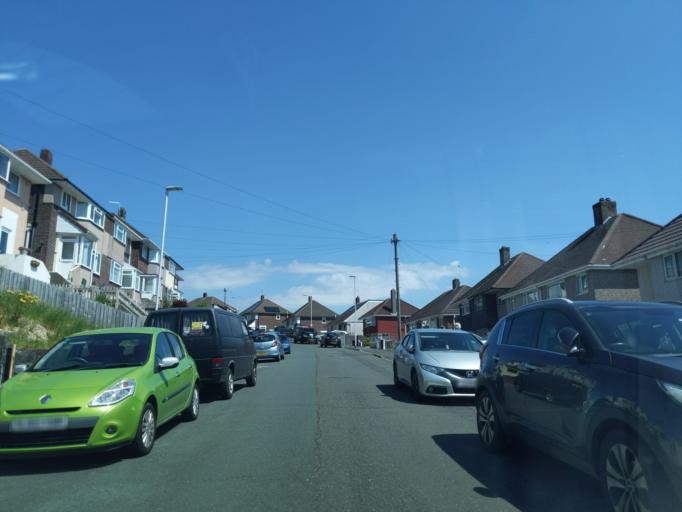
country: GB
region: England
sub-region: Cornwall
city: Torpoint
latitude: 50.4004
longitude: -4.1765
